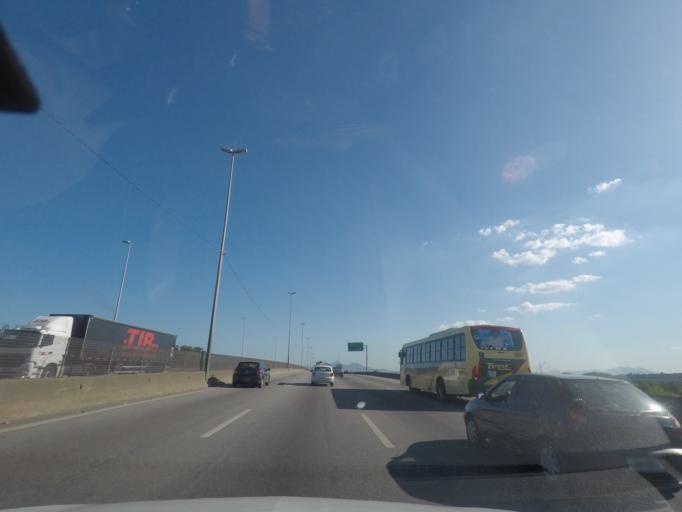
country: BR
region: Rio de Janeiro
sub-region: Duque De Caxias
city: Duque de Caxias
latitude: -22.7123
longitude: -43.2903
